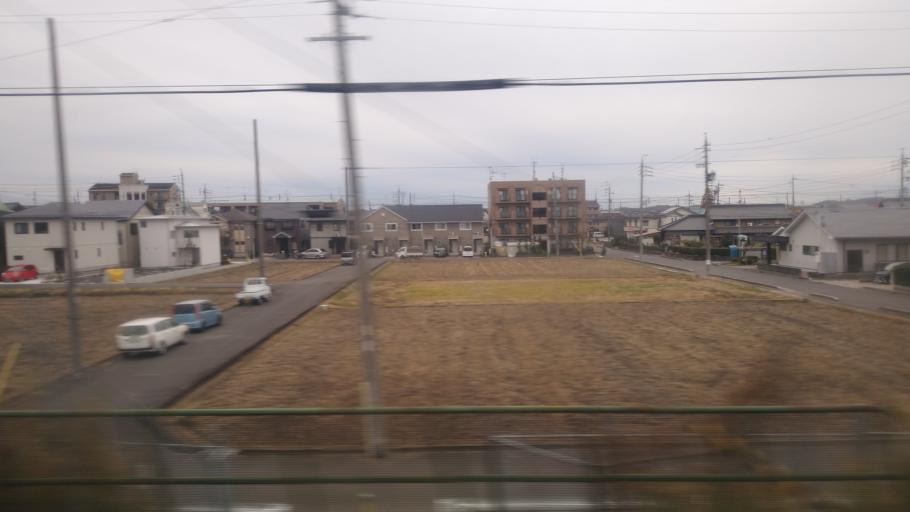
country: JP
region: Aichi
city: Kasugai
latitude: 35.2642
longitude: 137.0320
